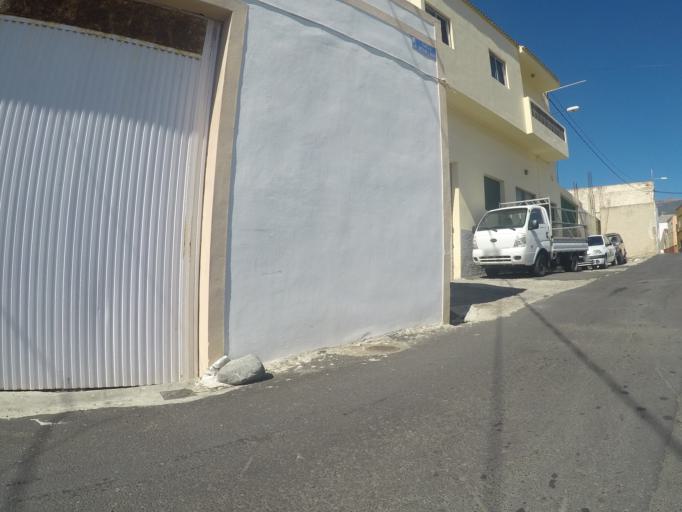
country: ES
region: Canary Islands
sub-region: Provincia de Santa Cruz de Tenerife
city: Lomo de Arico
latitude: 28.1815
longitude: -16.4845
